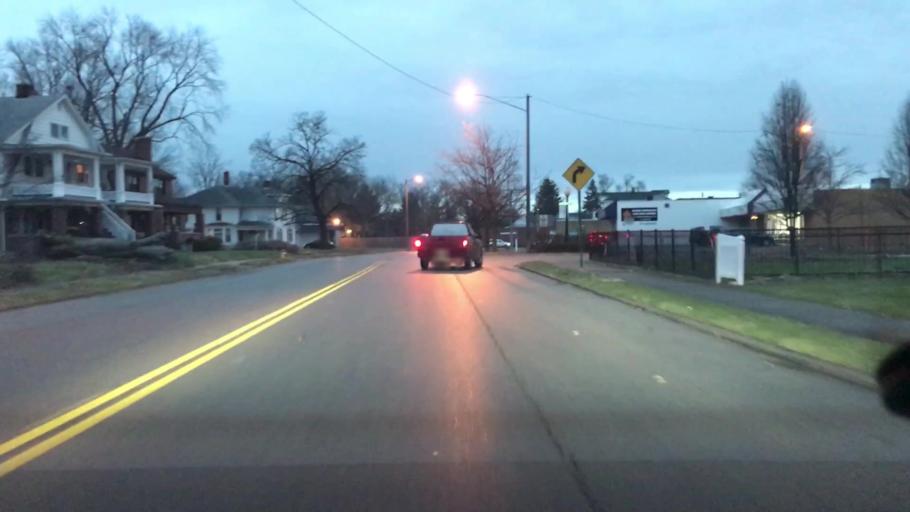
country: US
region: Ohio
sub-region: Clark County
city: Springfield
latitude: 39.9216
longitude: -83.7741
